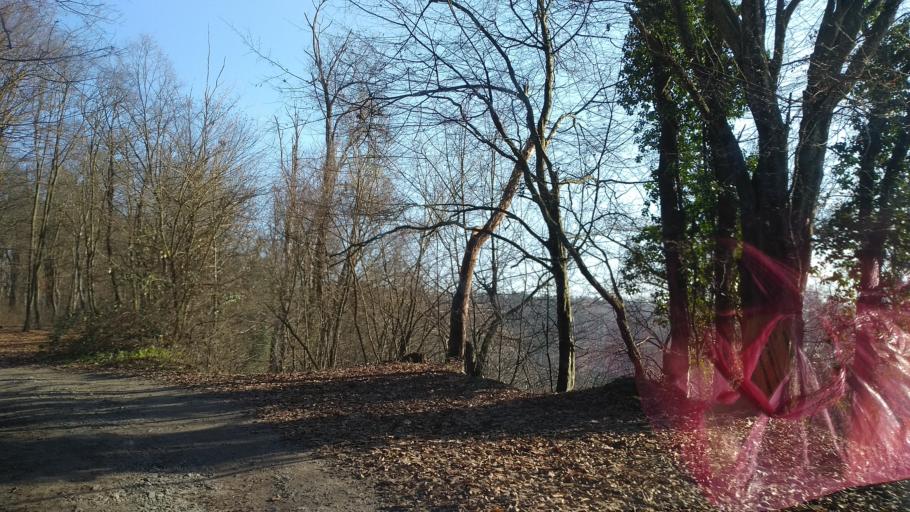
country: HU
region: Somogy
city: Barcs
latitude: 45.9526
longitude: 17.5164
